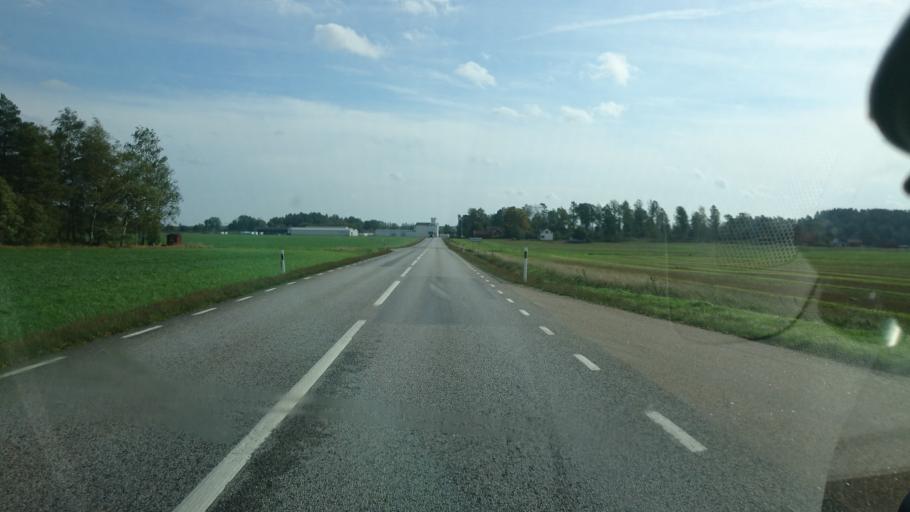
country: SE
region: Vaestra Goetaland
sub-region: Alingsas Kommun
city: Sollebrunn
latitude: 58.1245
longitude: 12.5063
